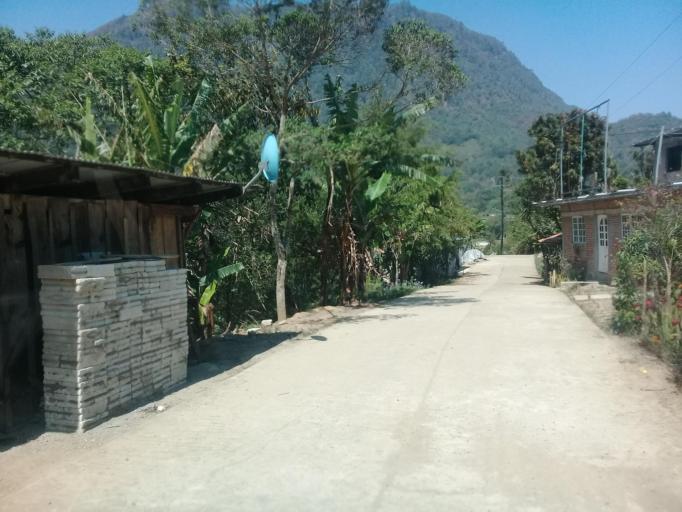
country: MX
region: Veracruz
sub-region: Tlilapan
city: Tonalixco
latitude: 18.7568
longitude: -97.0428
